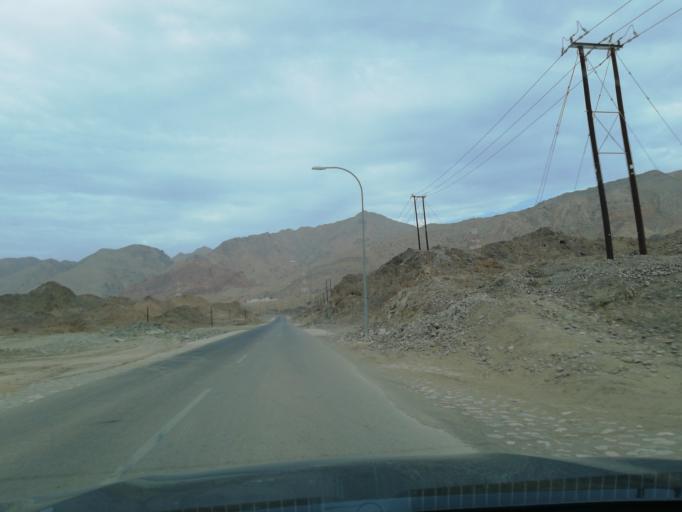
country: OM
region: Muhafazat Masqat
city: Bawshar
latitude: 23.4870
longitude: 58.3359
